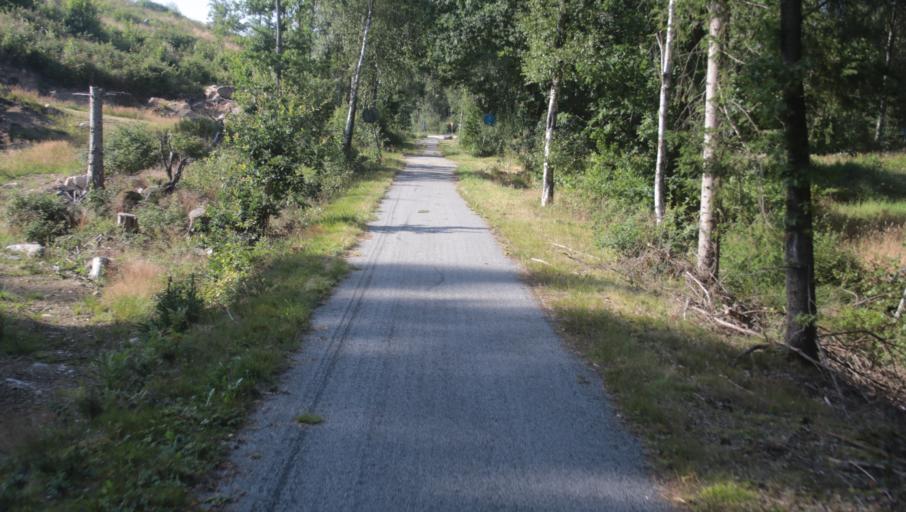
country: SE
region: Blekinge
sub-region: Karlshamns Kommun
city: Svangsta
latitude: 56.3183
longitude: 14.7079
